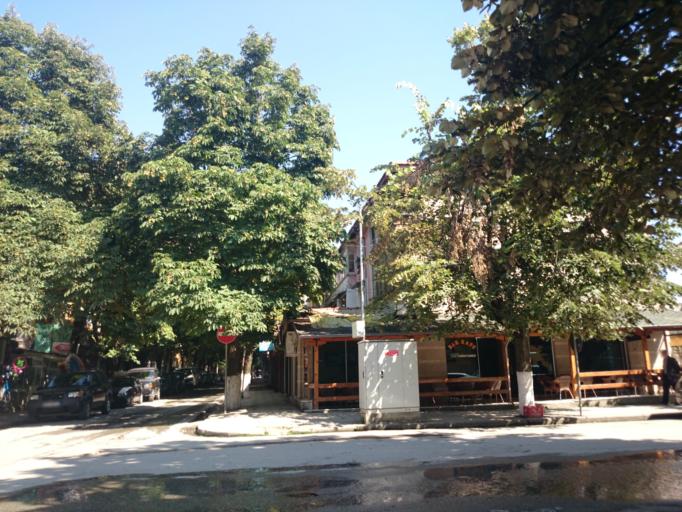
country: AL
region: Diber
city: Peshkopi
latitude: 41.6836
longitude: 20.4279
